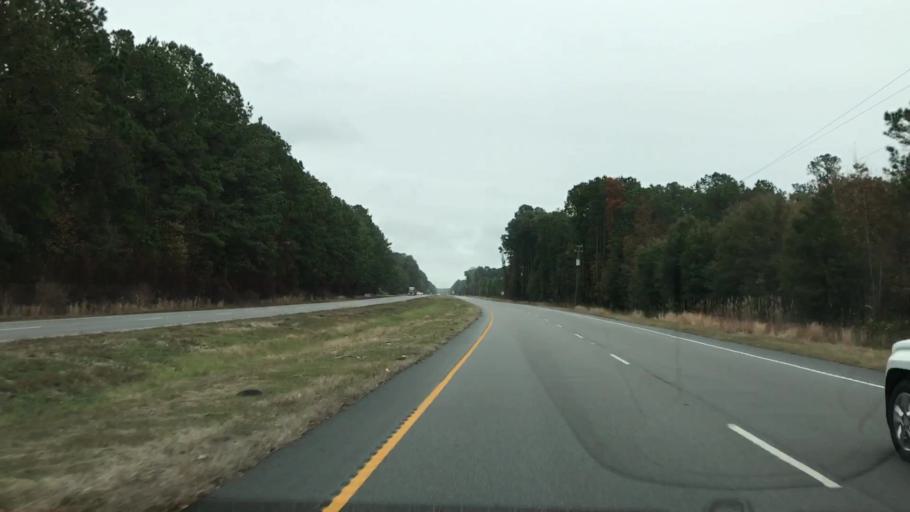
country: US
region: South Carolina
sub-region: Charleston County
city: Awendaw
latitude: 33.1021
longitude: -79.4667
